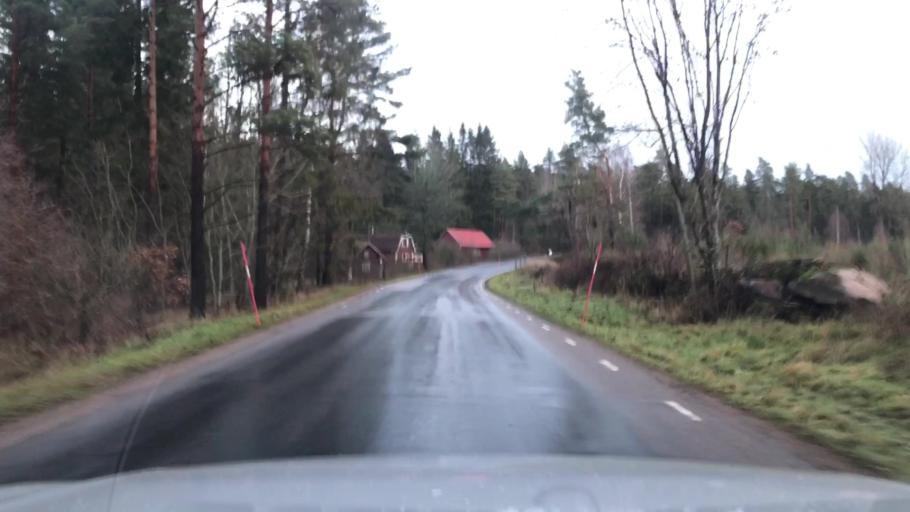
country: SE
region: OEstergoetland
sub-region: Linkopings Kommun
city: Linkoping
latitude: 58.3452
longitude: 15.6132
